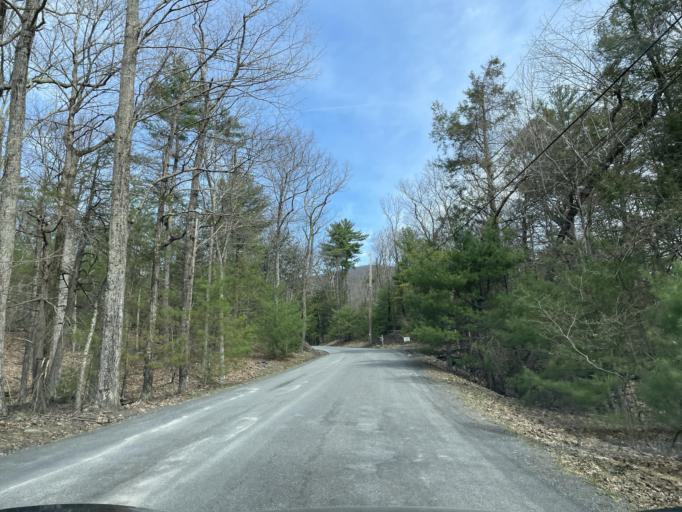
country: US
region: New York
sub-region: Ulster County
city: Woodstock
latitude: 42.0577
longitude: -74.0877
